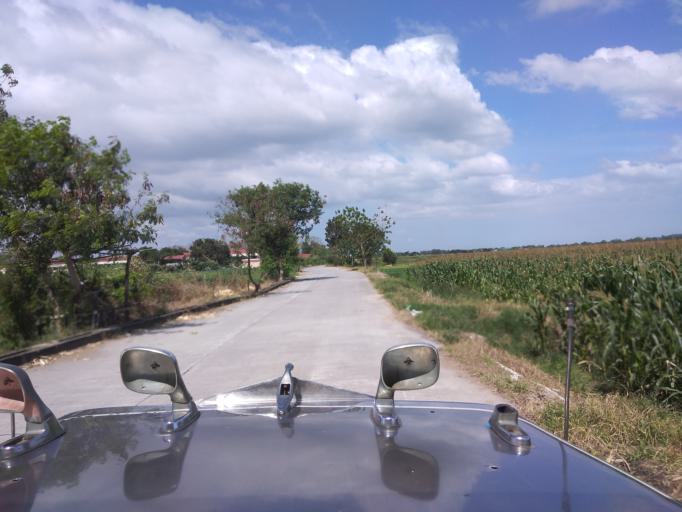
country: PH
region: Central Luzon
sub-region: Province of Pampanga
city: Anao
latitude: 15.1270
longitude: 120.7014
